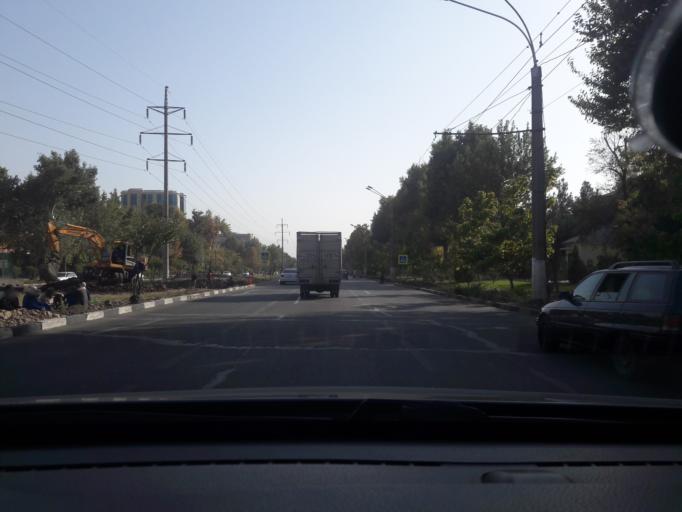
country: TJ
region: Dushanbe
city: Dushanbe
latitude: 38.5312
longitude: 68.7618
